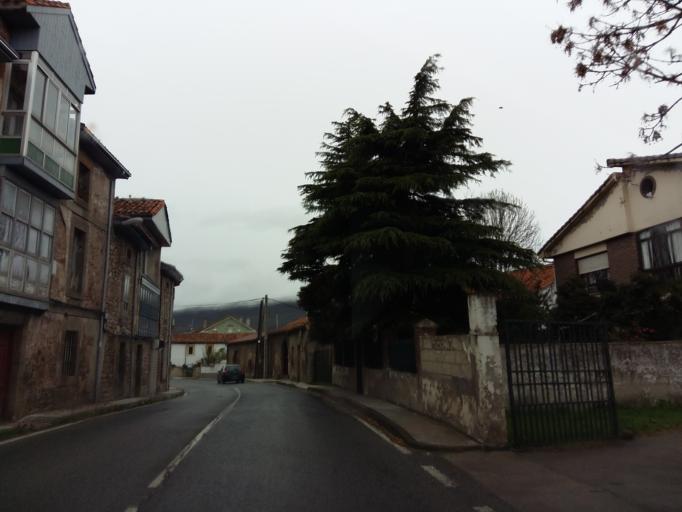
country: ES
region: Cantabria
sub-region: Provincia de Cantabria
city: Reinosa
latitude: 42.9810
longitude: -4.1491
